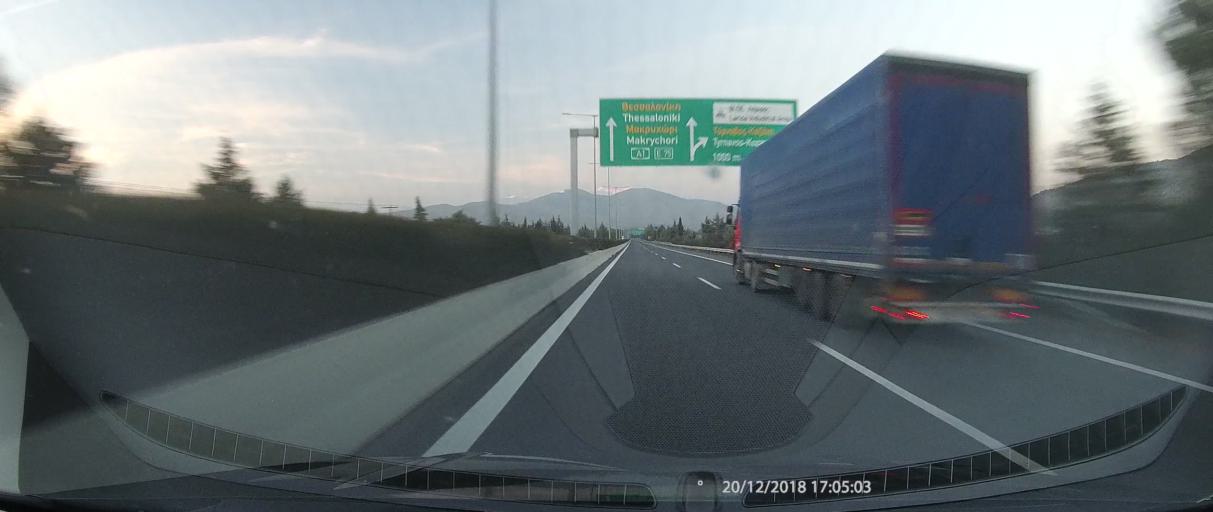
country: GR
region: Thessaly
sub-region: Nomos Larisis
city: Makrychori
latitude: 39.7311
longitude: 22.4786
